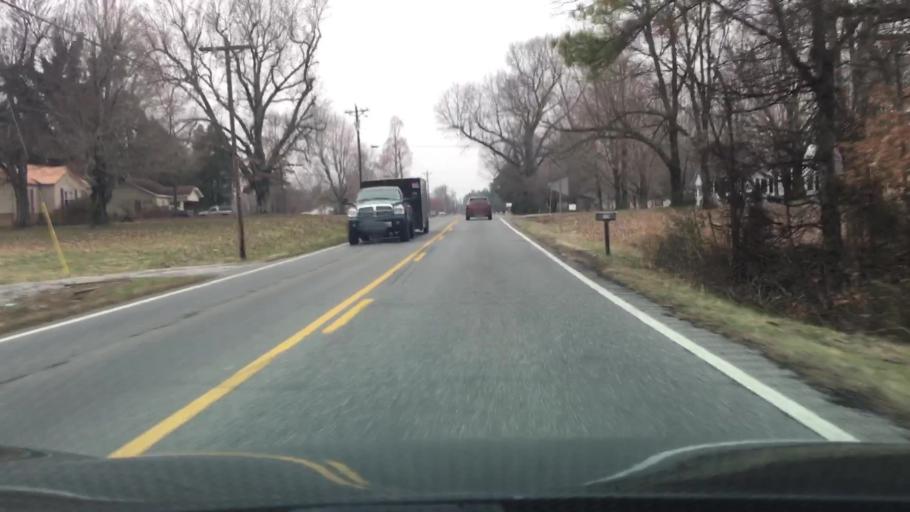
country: US
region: Kentucky
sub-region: Marshall County
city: Calvert City
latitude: 36.9719
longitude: -88.4098
